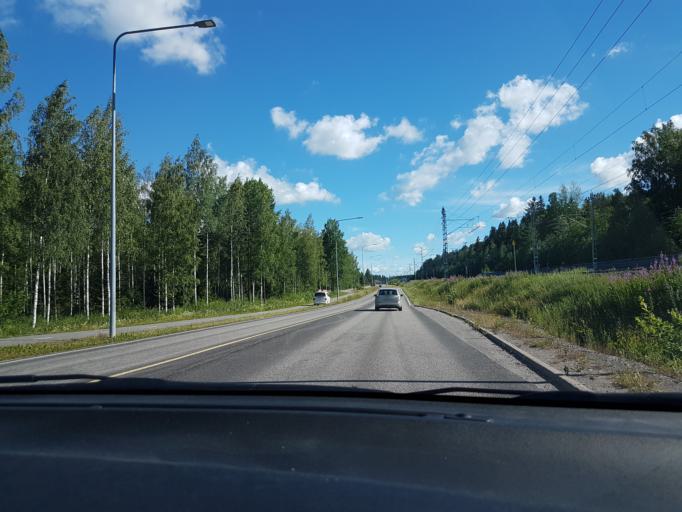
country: FI
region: Uusimaa
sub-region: Helsinki
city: Kerava
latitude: 60.3648
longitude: 25.0876
